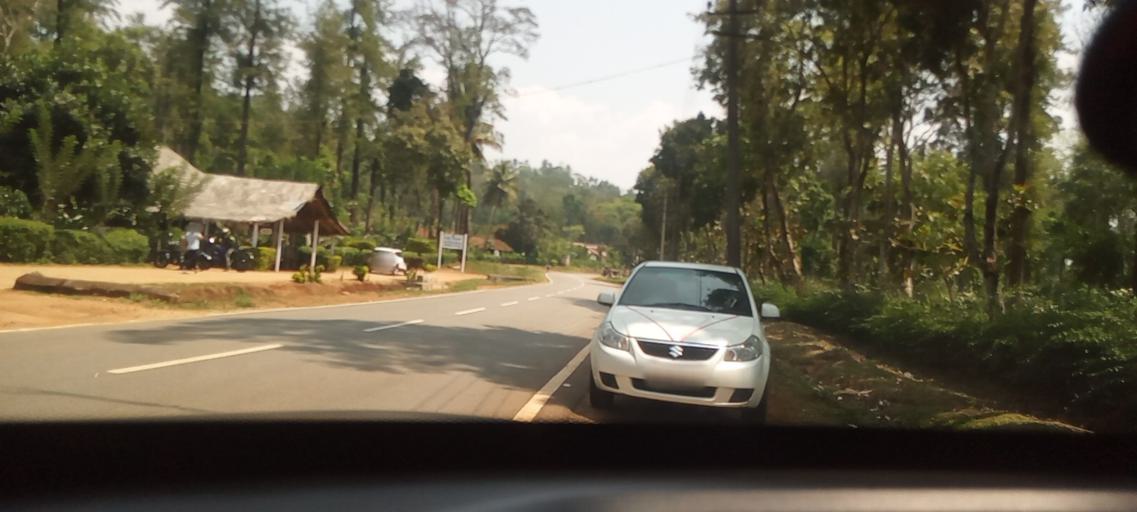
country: IN
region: Karnataka
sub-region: Chikmagalur
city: Koppa
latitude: 13.3523
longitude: 75.4731
